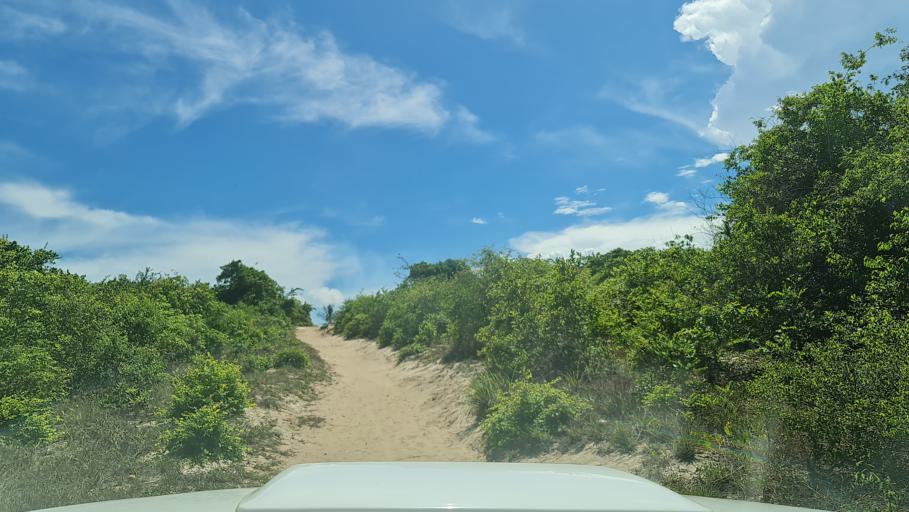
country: MZ
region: Nampula
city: Antonio Enes
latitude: -15.7043
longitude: 40.2634
